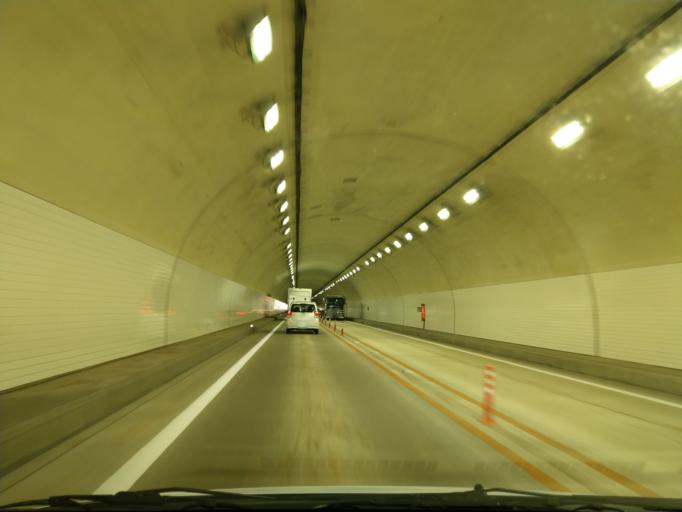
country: JP
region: Akita
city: Takanosu
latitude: 40.2191
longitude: 140.4267
